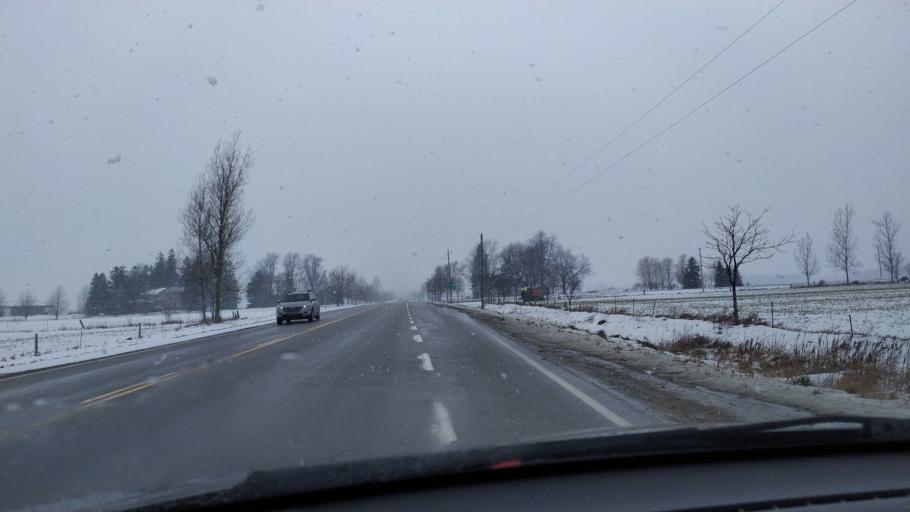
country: CA
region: Ontario
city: Stratford
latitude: 43.5060
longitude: -80.8881
